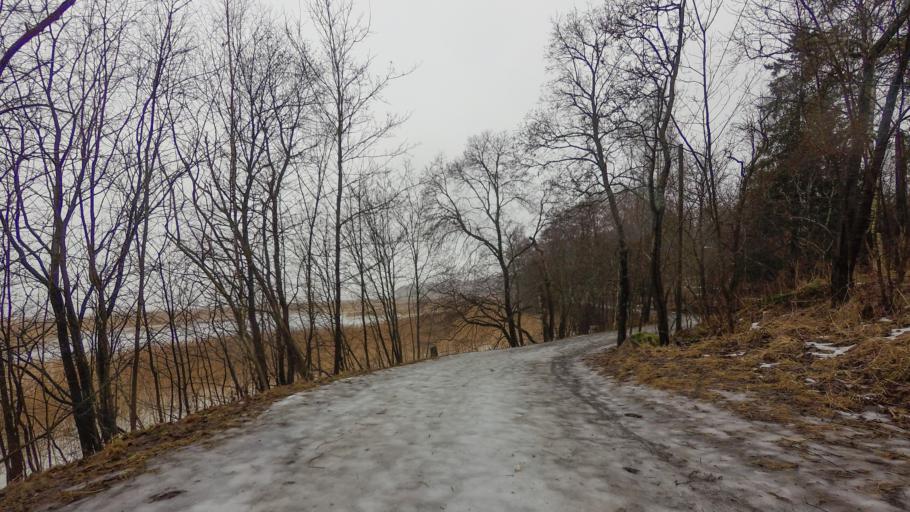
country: FI
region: Uusimaa
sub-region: Helsinki
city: Helsinki
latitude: 60.1979
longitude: 25.0252
